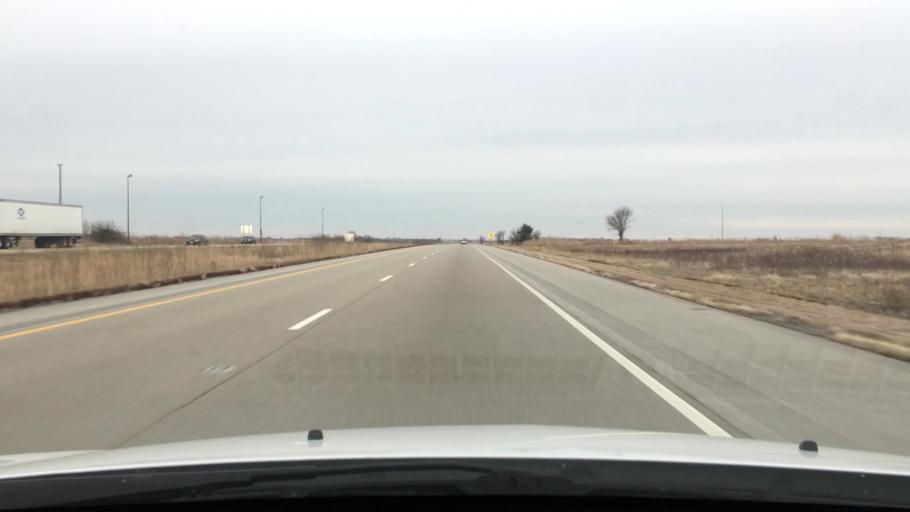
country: US
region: Illinois
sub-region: Logan County
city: Atlanta
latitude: 40.2604
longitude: -89.2190
